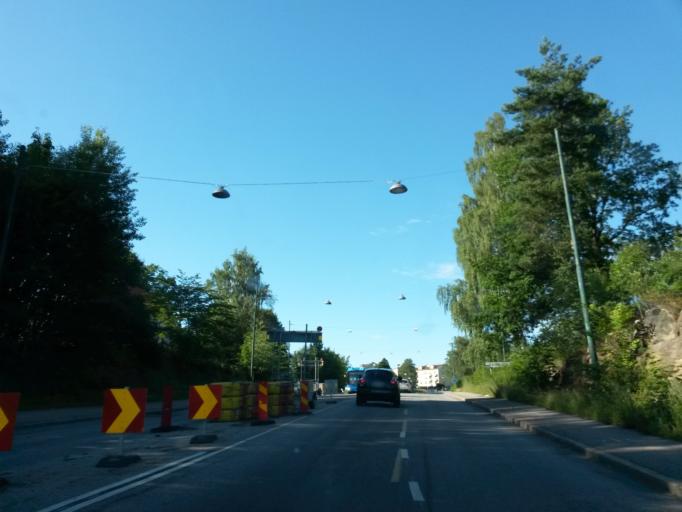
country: SE
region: Vaestra Goetaland
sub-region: Boras Kommun
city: Boras
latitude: 57.7419
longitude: 12.9382
